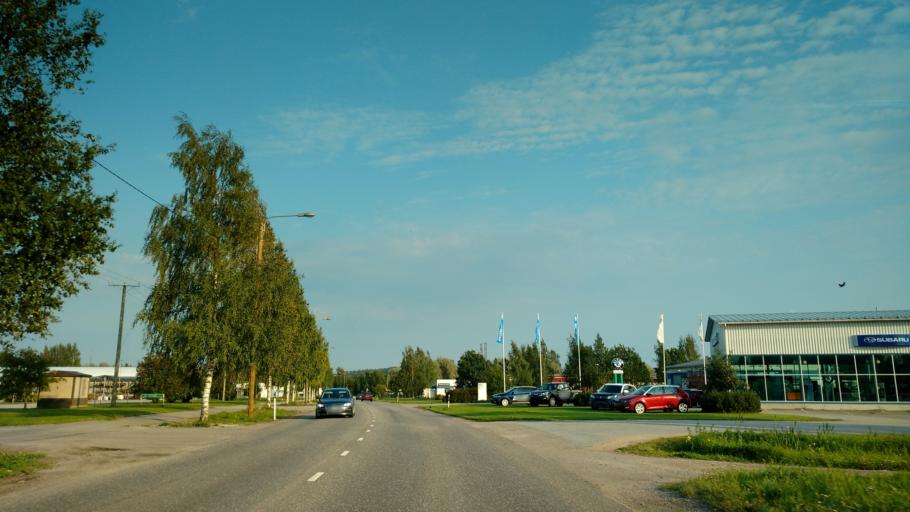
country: FI
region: Varsinais-Suomi
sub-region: Salo
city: Salo
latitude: 60.3780
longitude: 23.1062
